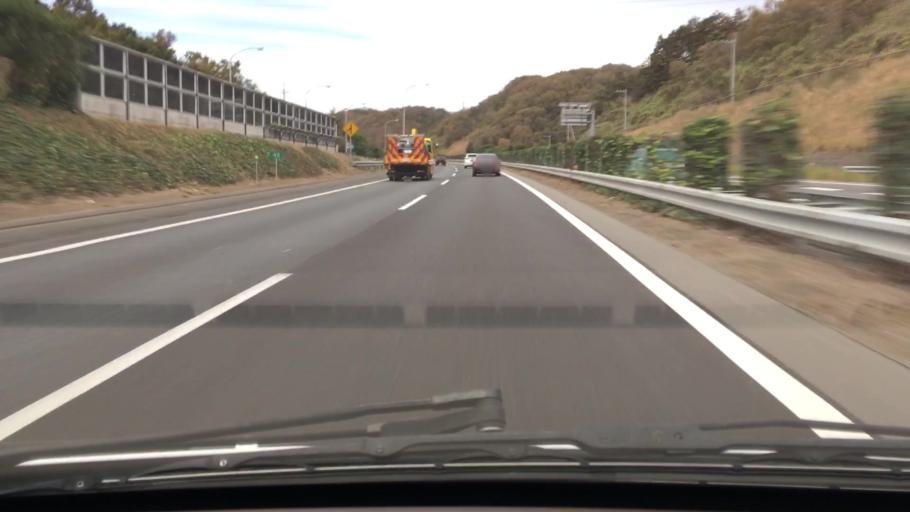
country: JP
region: Chiba
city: Ichihara
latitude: 35.4612
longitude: 140.0857
